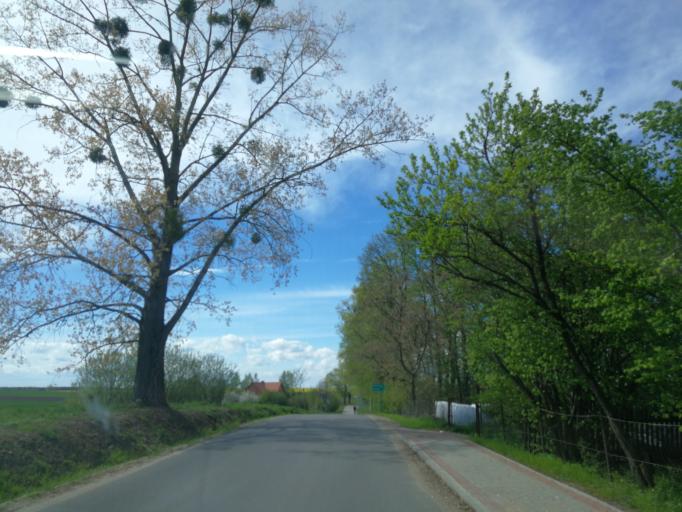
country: PL
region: Warmian-Masurian Voivodeship
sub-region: Powiat ilawski
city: Lubawa
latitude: 53.6003
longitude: 19.6922
